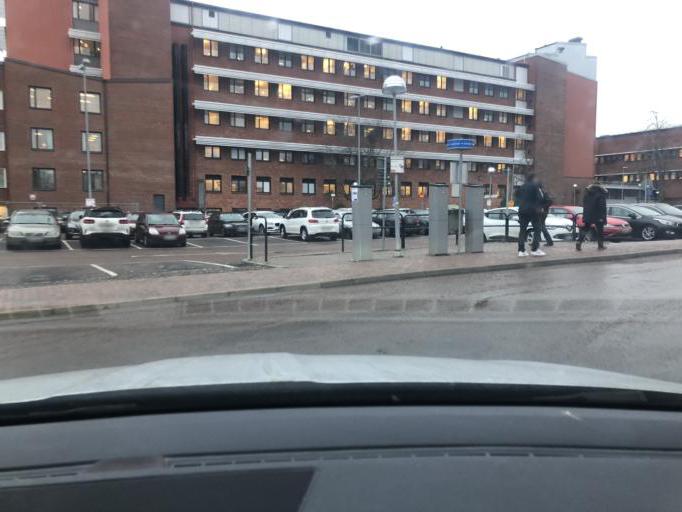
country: SE
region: Vaermland
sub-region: Karlstads Kommun
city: Karlstad
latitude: 59.3740
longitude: 13.4803
